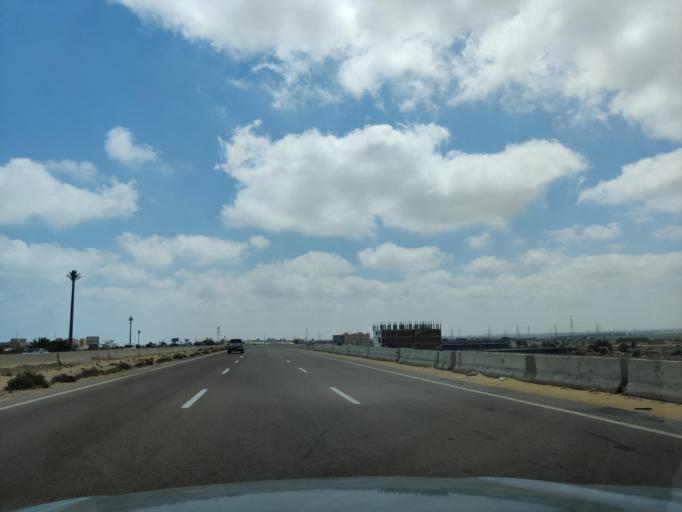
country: EG
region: Muhafazat Matruh
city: Al `Alamayn
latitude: 30.8232
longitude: 29.1823
